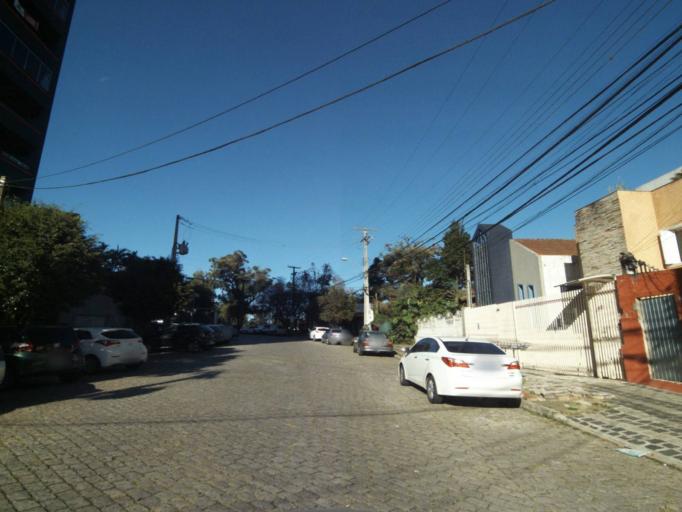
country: BR
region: Parana
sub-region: Curitiba
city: Curitiba
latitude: -25.4124
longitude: -49.2559
